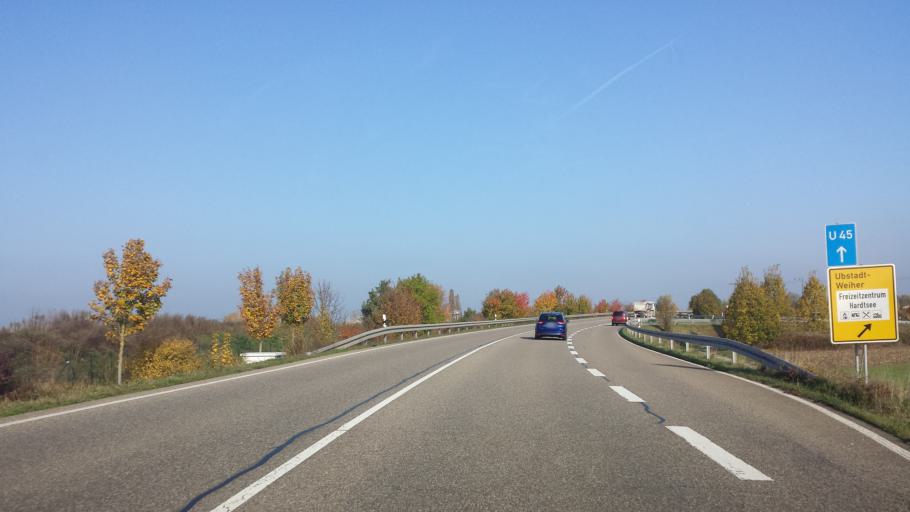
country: DE
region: Baden-Wuerttemberg
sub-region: Karlsruhe Region
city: Ubstadt-Weiher
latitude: 49.1658
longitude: 8.6186
